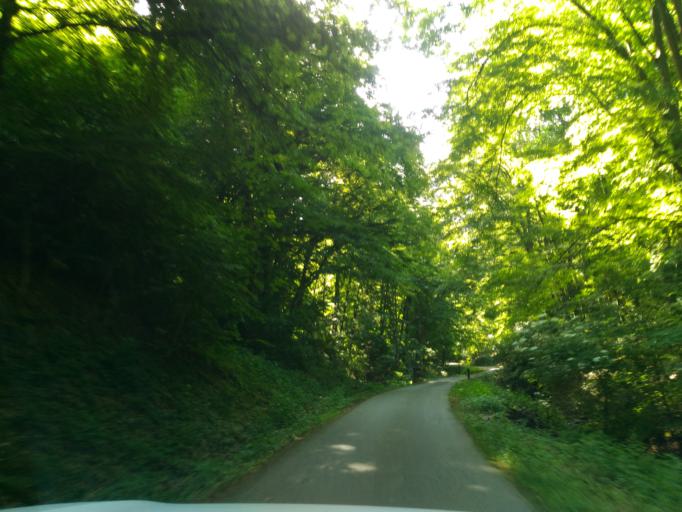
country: HU
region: Baranya
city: Hosszuheteny
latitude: 46.2190
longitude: 18.3512
